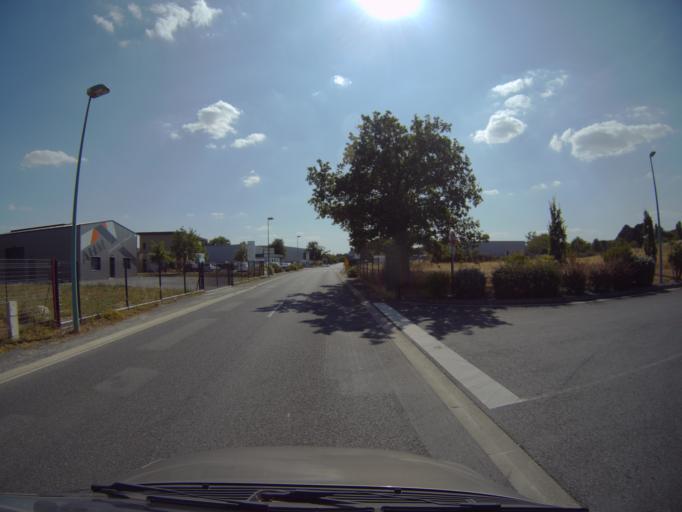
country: FR
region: Pays de la Loire
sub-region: Departement de la Loire-Atlantique
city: Aigrefeuille-sur-Maine
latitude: 47.0774
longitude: -1.4160
